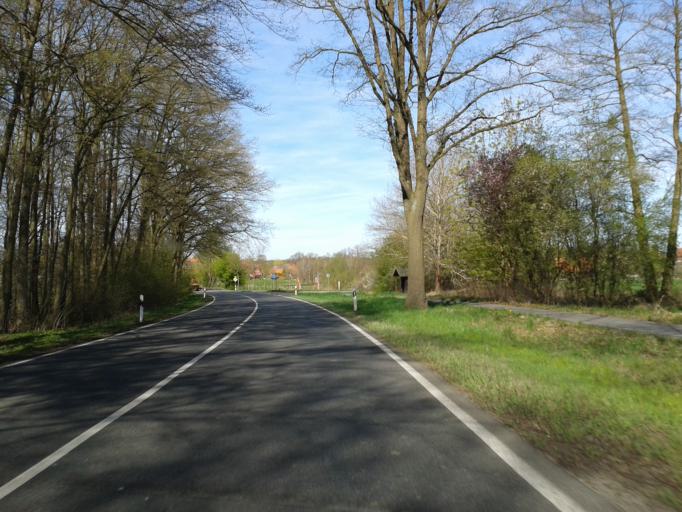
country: DE
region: Lower Saxony
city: Schwienau
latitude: 52.9606
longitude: 10.4663
